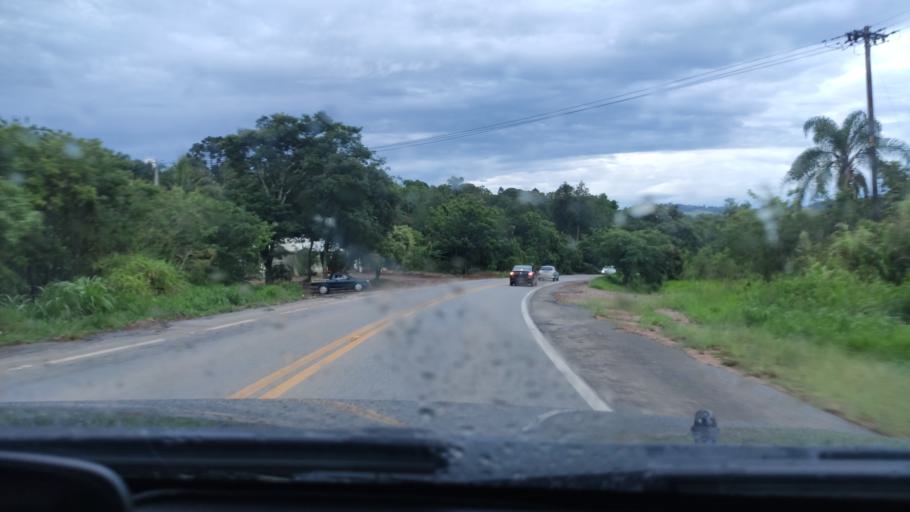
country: BR
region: Sao Paulo
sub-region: Braganca Paulista
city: Braganca Paulista
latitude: -22.7813
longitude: -46.5632
